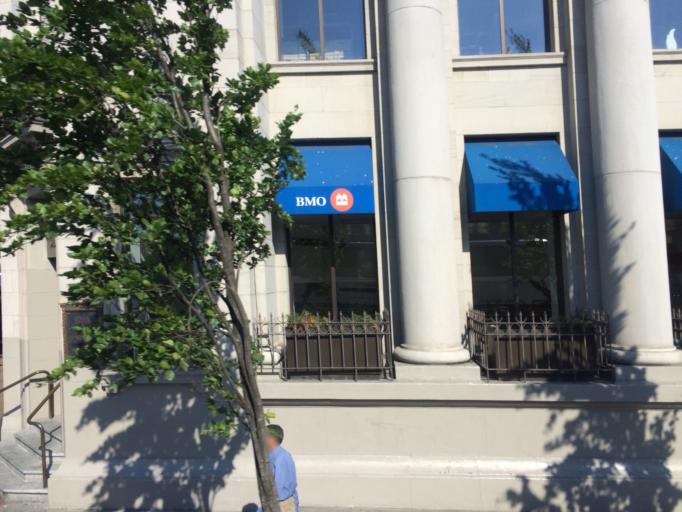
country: CA
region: British Columbia
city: Victoria
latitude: 48.4260
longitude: -123.3648
